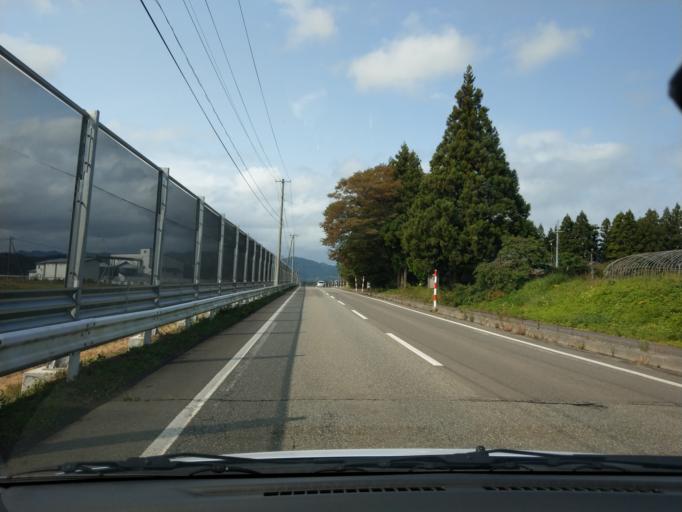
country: JP
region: Akita
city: Omagari
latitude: 39.5250
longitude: 140.2680
